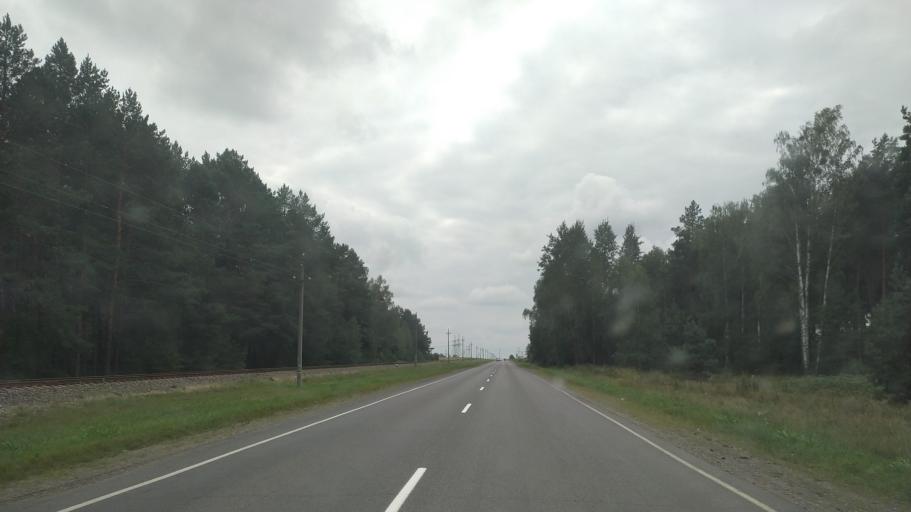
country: BY
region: Brest
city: Byelaazyorsk
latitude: 52.5246
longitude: 25.1480
